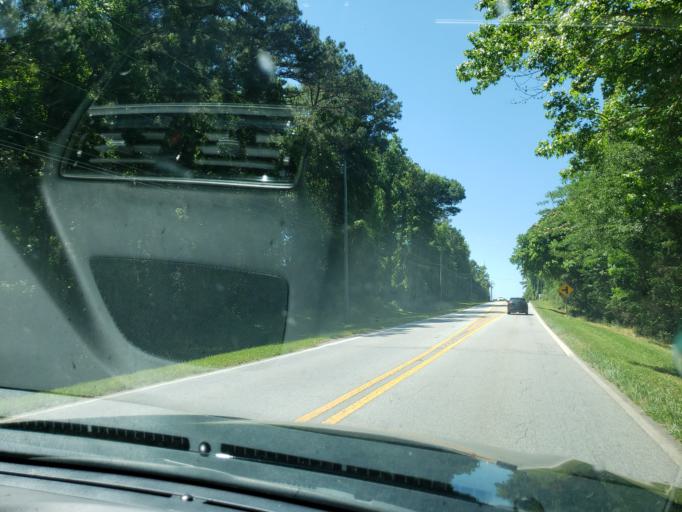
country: US
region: Alabama
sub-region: Lee County
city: Auburn
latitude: 32.6422
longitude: -85.4814
